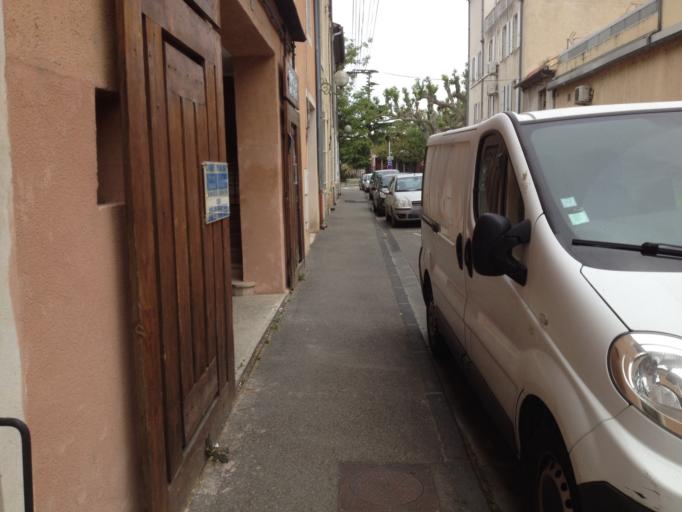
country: FR
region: Provence-Alpes-Cote d'Azur
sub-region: Departement du Vaucluse
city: Orange
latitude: 44.1357
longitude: 4.8044
